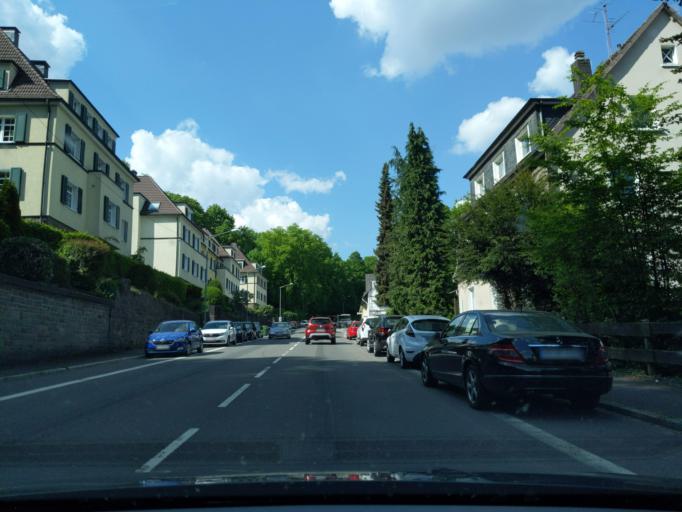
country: DE
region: North Rhine-Westphalia
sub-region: Regierungsbezirk Koln
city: Gummersbach
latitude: 51.0210
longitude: 7.5716
